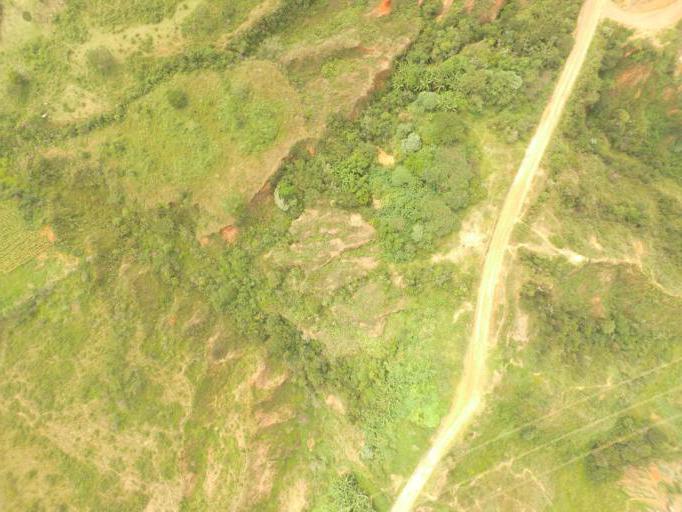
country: BR
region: Minas Gerais
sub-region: Tiradentes
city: Tiradentes
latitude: -21.0501
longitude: -44.0734
